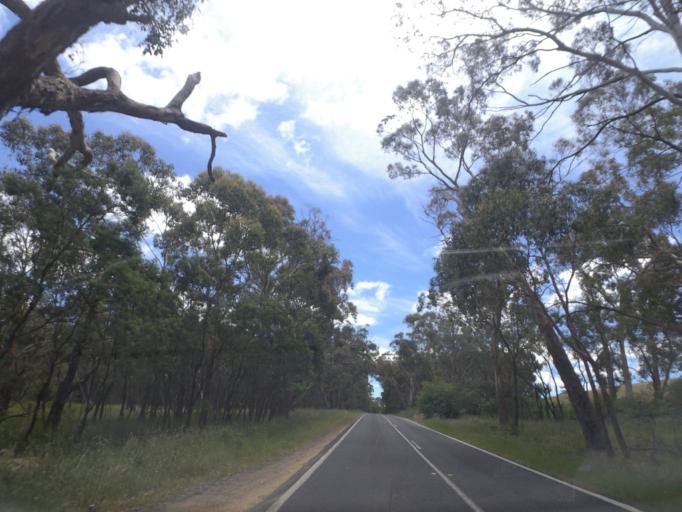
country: AU
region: Victoria
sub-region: Mount Alexander
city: Castlemaine
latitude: -37.3278
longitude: 144.1651
